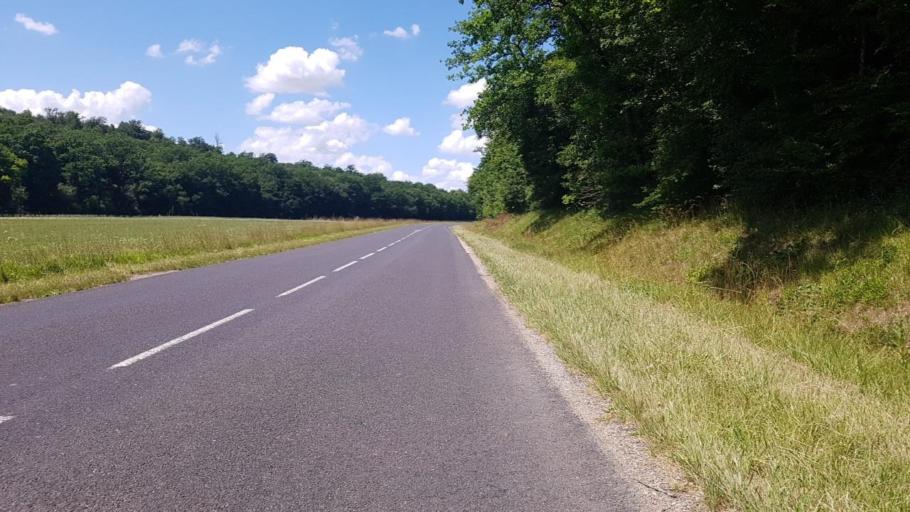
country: FR
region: Lorraine
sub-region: Departement de la Meuse
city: Vacon
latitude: 48.6730
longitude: 5.5883
